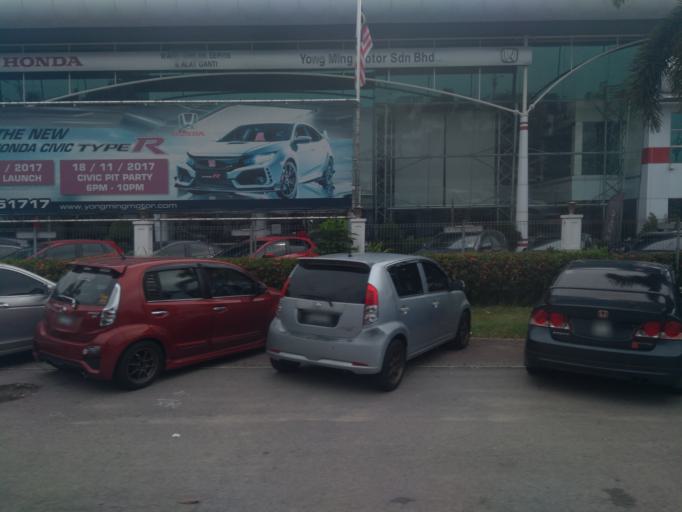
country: MY
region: Johor
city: Johor Bahru
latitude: 1.4904
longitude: 103.7101
